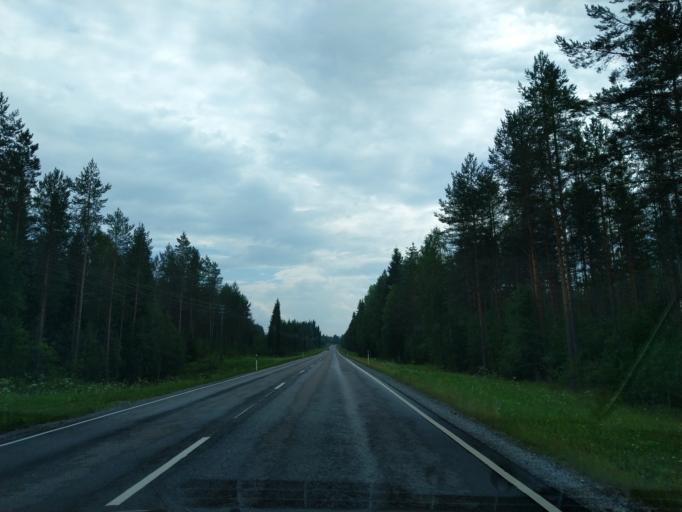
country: FI
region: Southern Savonia
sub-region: Savonlinna
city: Punkaharju
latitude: 61.6480
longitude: 29.4234
